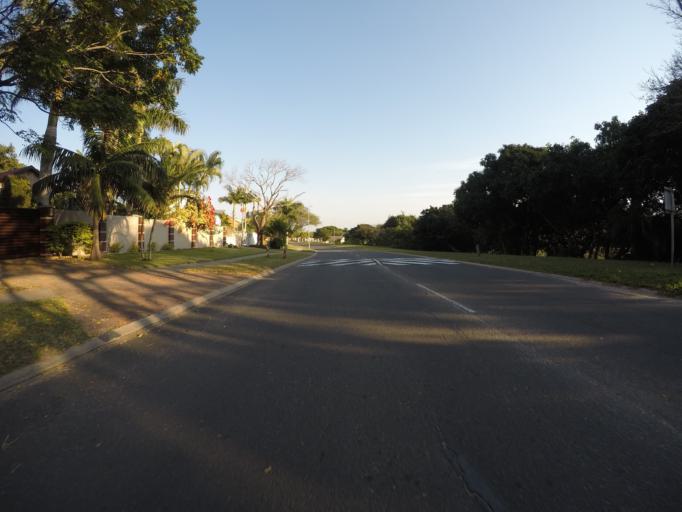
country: ZA
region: KwaZulu-Natal
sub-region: uThungulu District Municipality
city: Richards Bay
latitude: -28.7732
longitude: 32.1144
